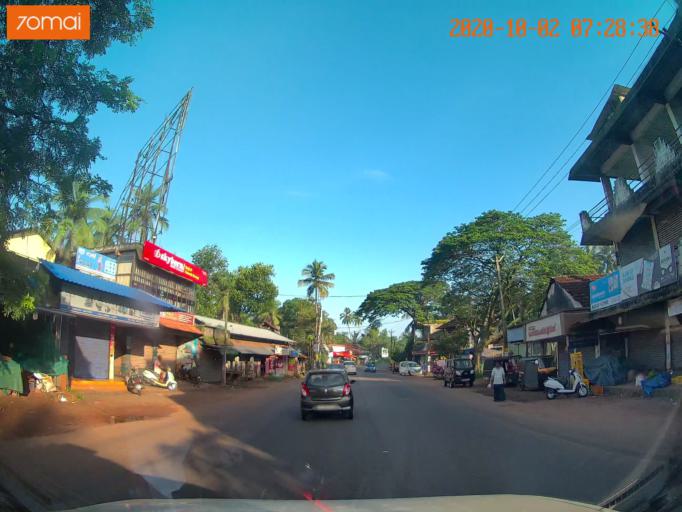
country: IN
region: Kerala
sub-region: Malappuram
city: Pariyapuram
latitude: 11.0294
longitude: 75.9420
